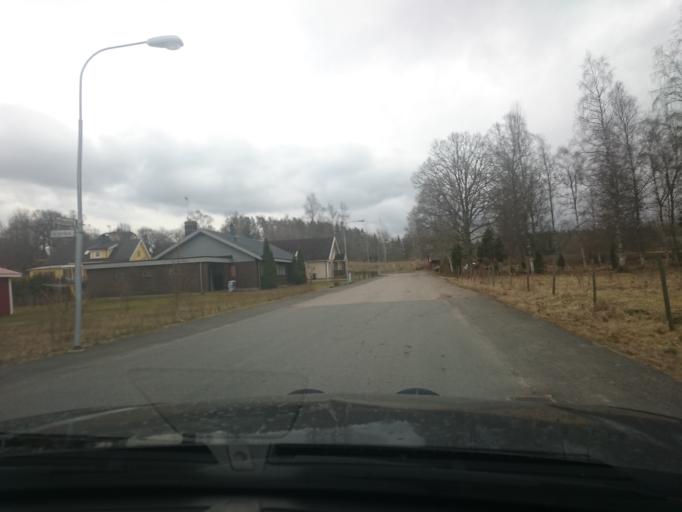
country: SE
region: Joenkoeping
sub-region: Vetlanda Kommun
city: Vetlanda
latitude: 57.2957
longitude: 15.1250
